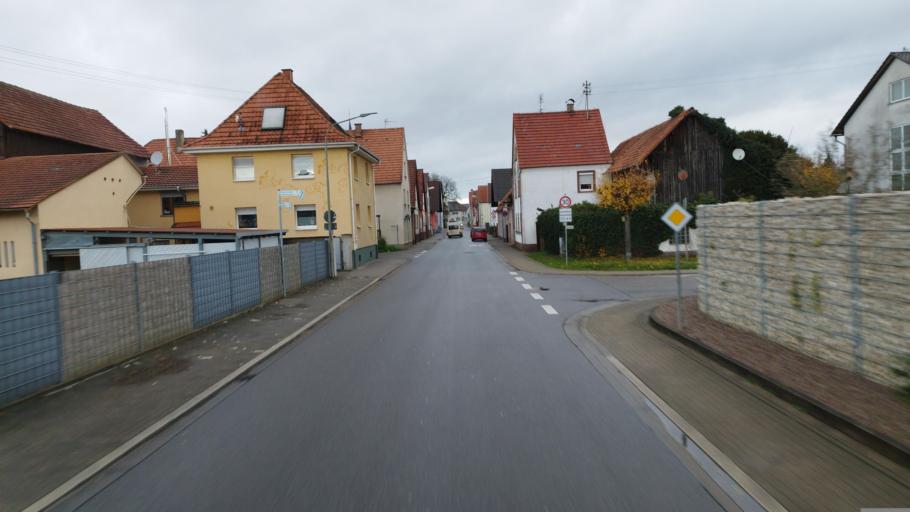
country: DE
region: Rheinland-Pfalz
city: Hatzenbuhl
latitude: 49.1083
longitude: 8.2452
